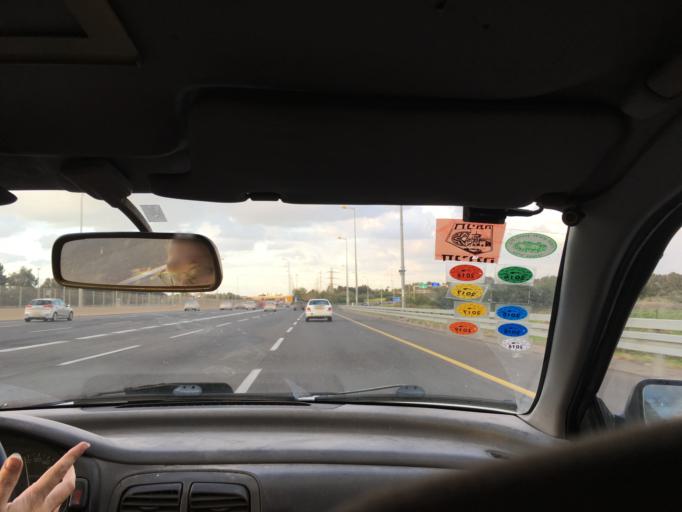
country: IL
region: Tel Aviv
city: Ramat HaSharon
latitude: 32.1323
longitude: 34.8106
